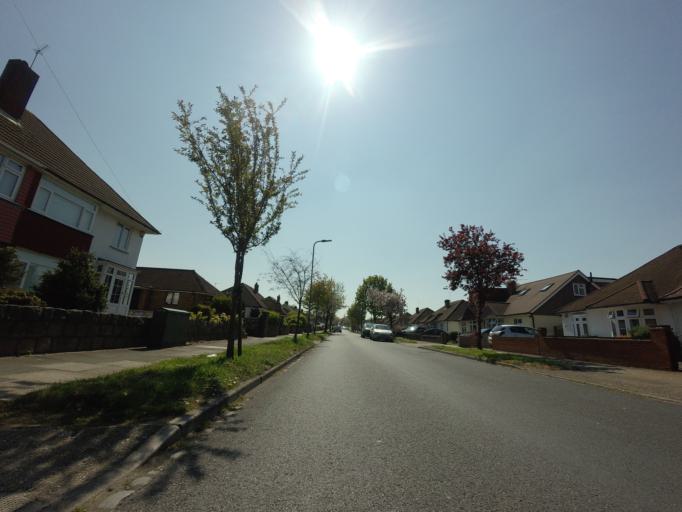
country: GB
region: England
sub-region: Greater London
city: Orpington
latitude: 51.3797
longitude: 0.1103
